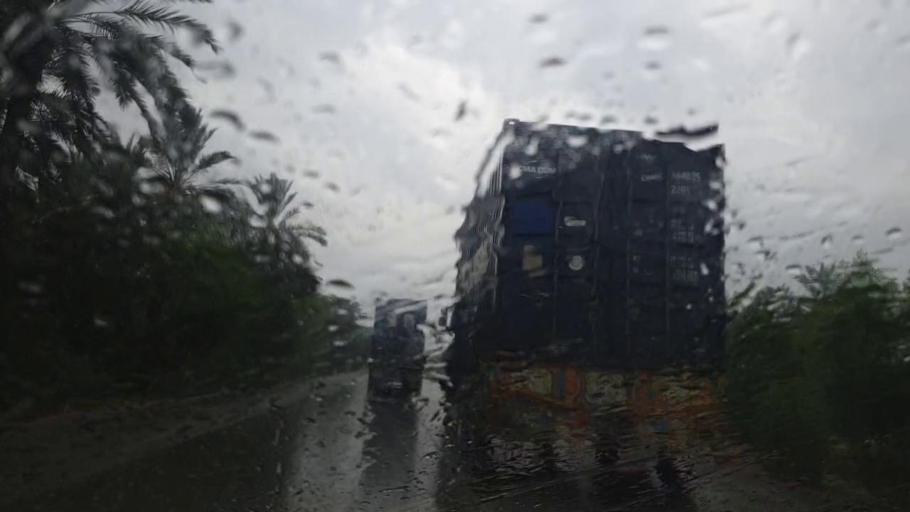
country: PK
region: Sindh
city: Khairpur
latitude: 27.5782
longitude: 68.7549
